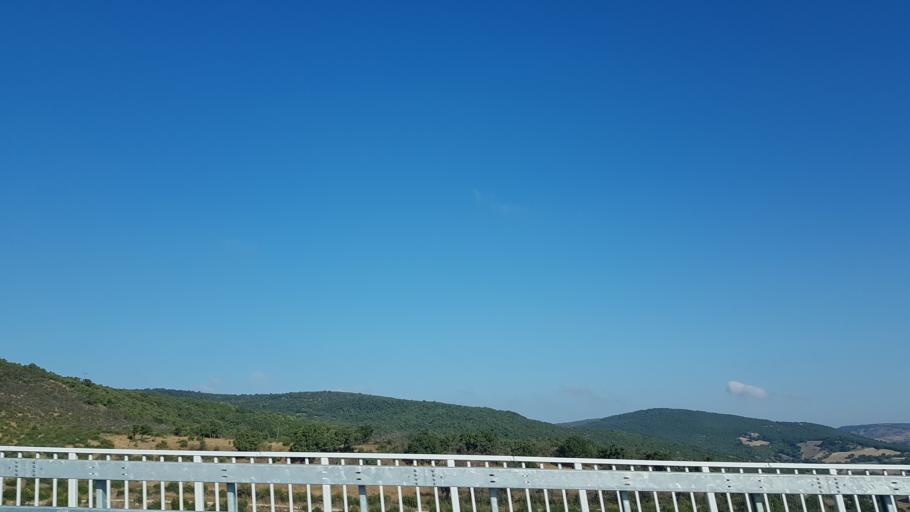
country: TR
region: Balikesir
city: Ertugrul
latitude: 39.5574
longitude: 27.6991
